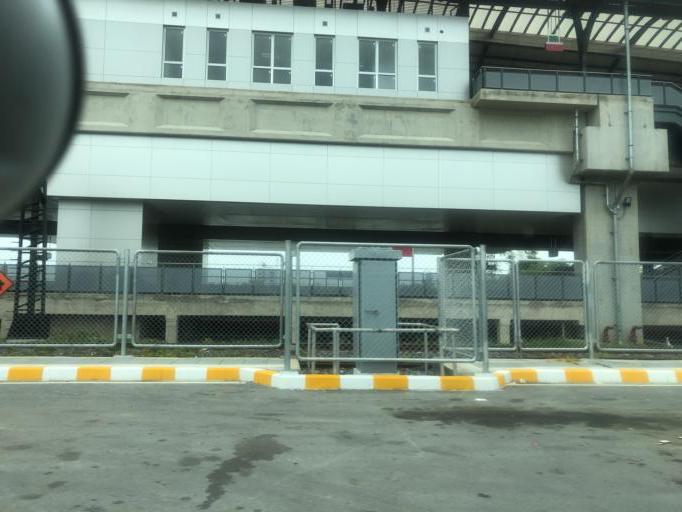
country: TH
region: Bangkok
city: Don Mueang
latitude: 13.9657
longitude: 100.6050
